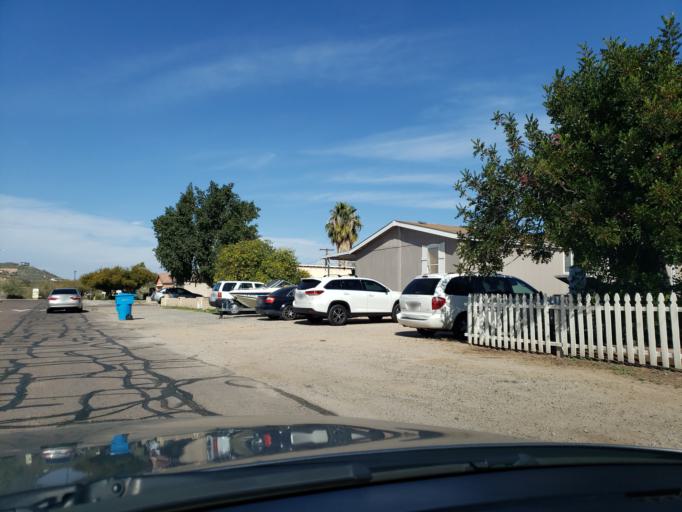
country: US
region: Arizona
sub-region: Maricopa County
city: Paradise Valley
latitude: 33.6468
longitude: -112.0352
